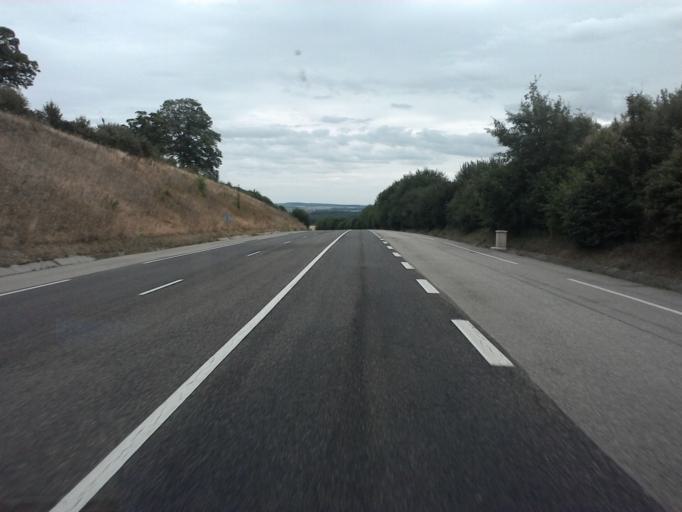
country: FR
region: Lorraine
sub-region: Departement de Meurthe-et-Moselle
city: Bainville-sur-Madon
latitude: 48.5801
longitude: 6.0288
